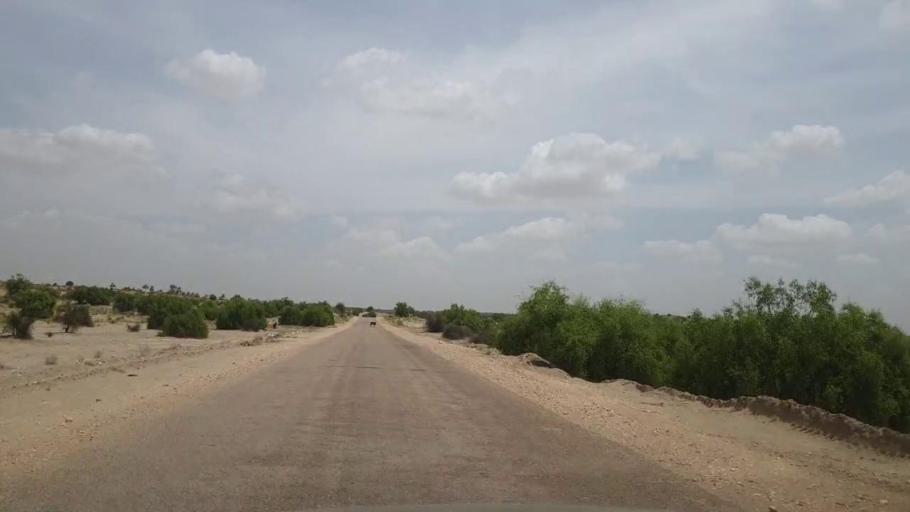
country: PK
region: Sindh
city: Kot Diji
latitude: 27.1901
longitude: 69.1682
